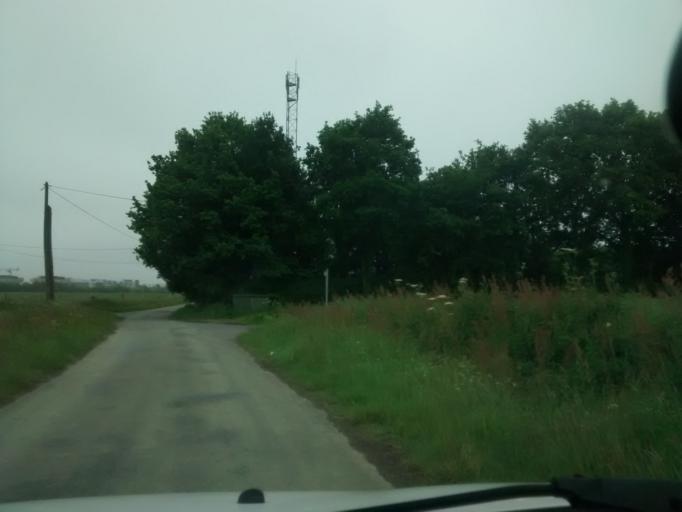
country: FR
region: Brittany
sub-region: Departement d'Ille-et-Vilaine
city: Montgermont
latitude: 48.1395
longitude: -1.7068
